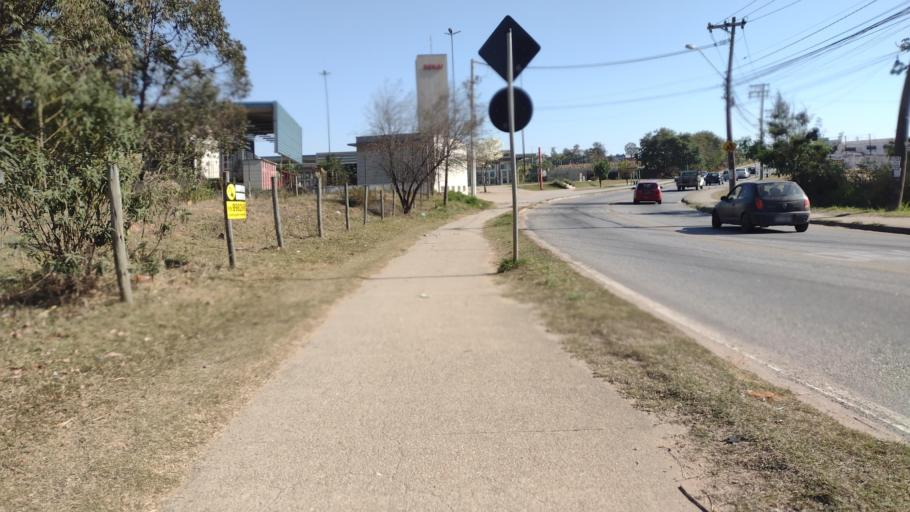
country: BR
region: Sao Paulo
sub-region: Sorocaba
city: Sorocaba
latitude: -23.4299
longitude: -47.4827
